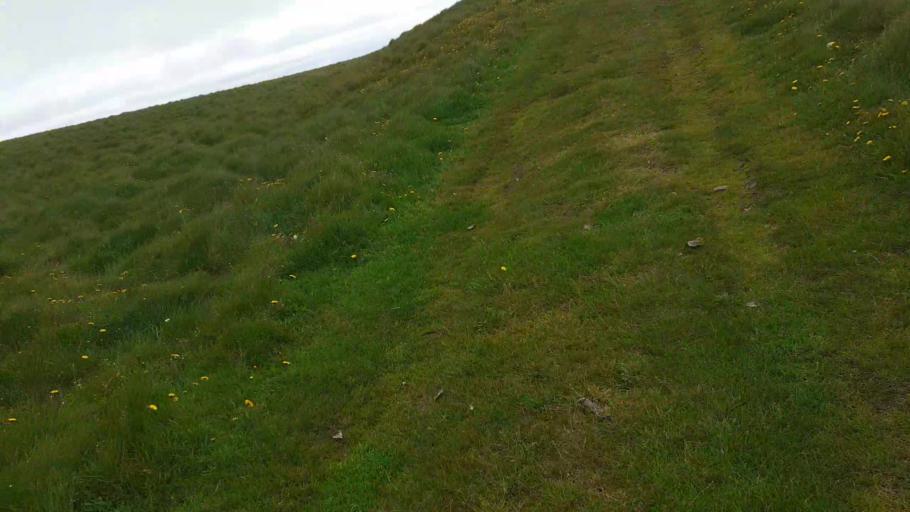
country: IS
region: Northeast
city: Dalvik
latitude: 66.5427
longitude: -17.9840
